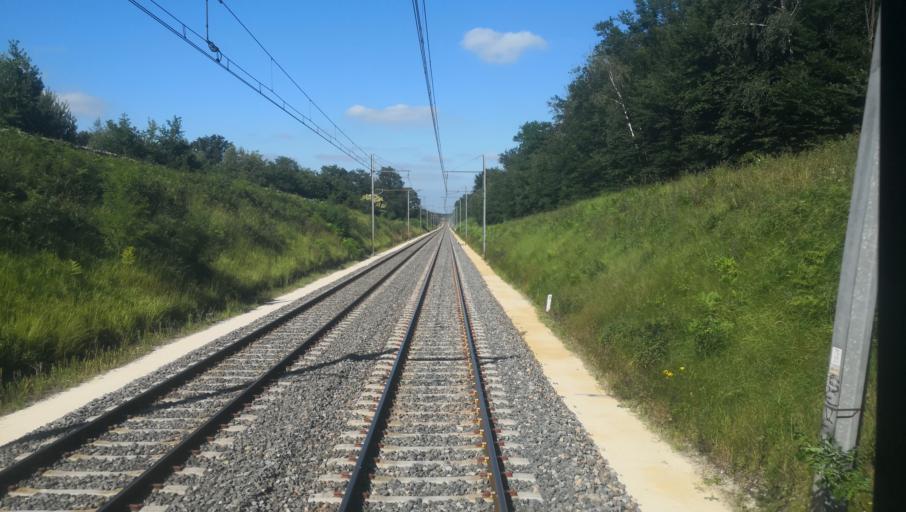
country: FR
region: Ile-de-France
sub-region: Departement de Seine-et-Marne
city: Veneux-les-Sablons
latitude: 48.3534
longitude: 2.7872
